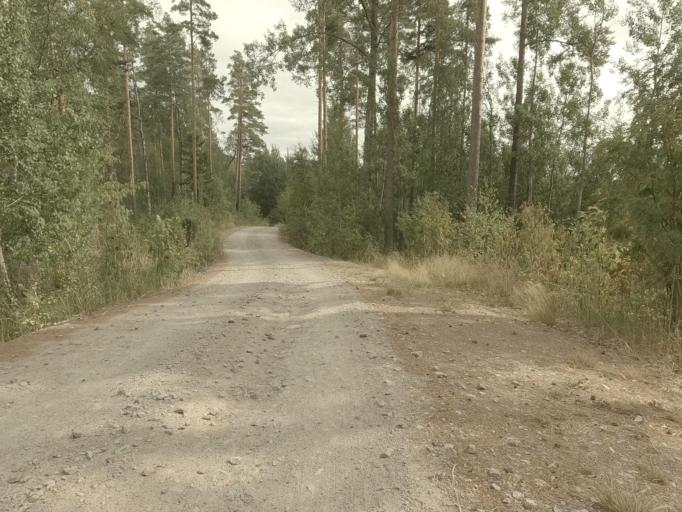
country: RU
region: Leningrad
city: Kamennogorsk
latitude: 60.9759
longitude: 29.1735
